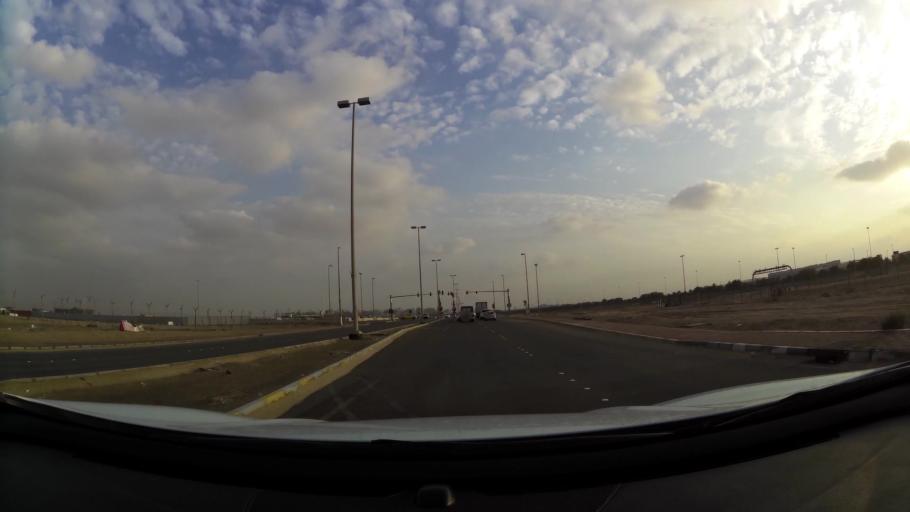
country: AE
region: Abu Dhabi
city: Abu Dhabi
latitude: 24.3615
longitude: 54.5281
